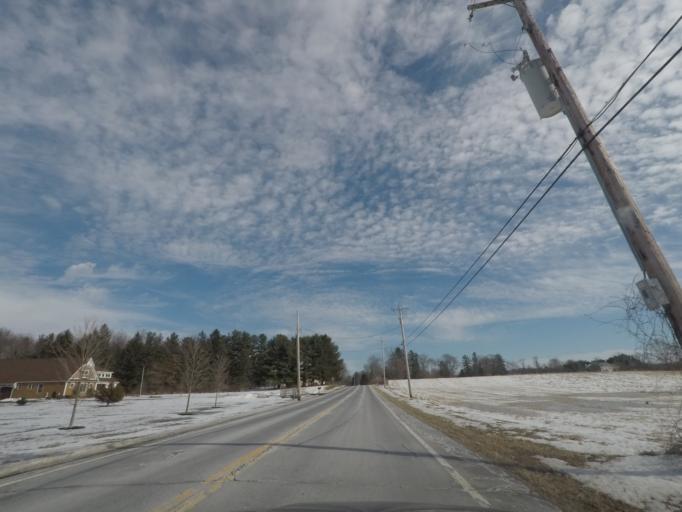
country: US
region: New York
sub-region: Albany County
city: Voorheesville
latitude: 42.6541
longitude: -73.9650
